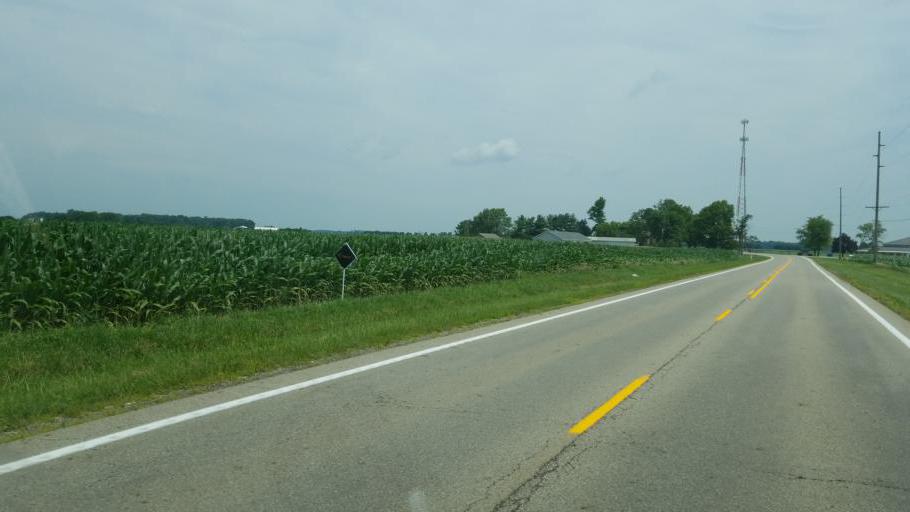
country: US
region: Ohio
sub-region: Madison County
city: West Jefferson
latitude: 40.0128
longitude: -83.3086
